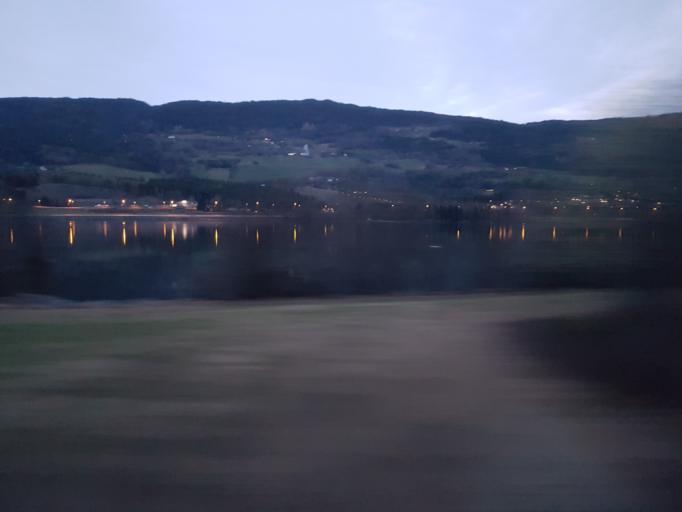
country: NO
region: Oppland
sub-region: Oyer
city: Tretten
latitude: 61.2528
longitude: 10.4211
